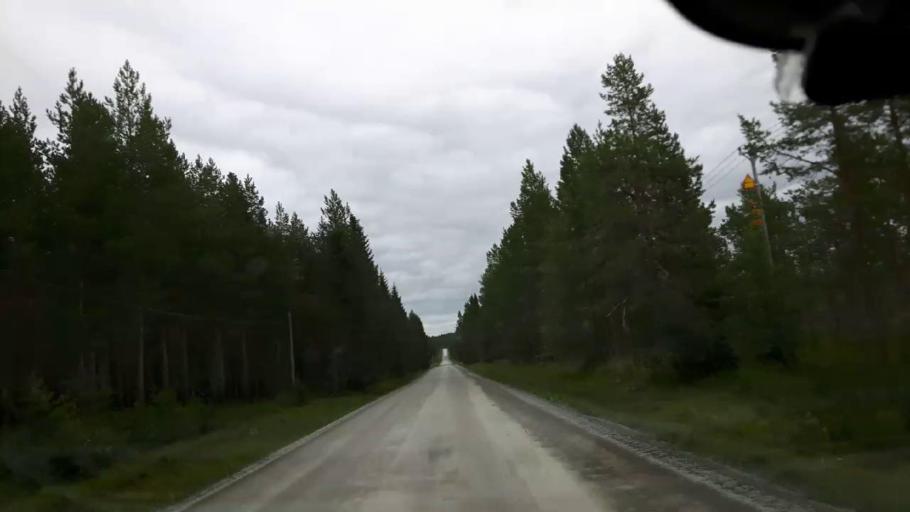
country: SE
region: Jaemtland
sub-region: OEstersunds Kommun
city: Brunflo
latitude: 63.0999
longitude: 15.1151
